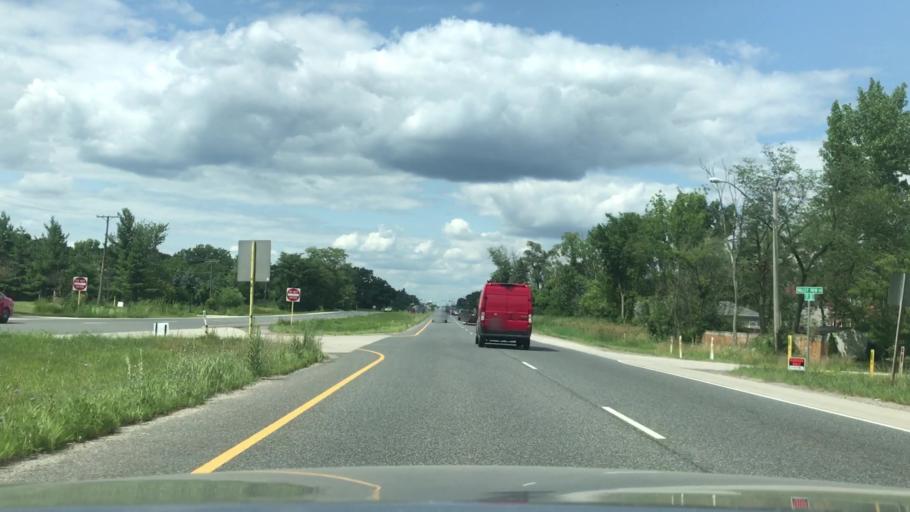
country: US
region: Illinois
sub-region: DuPage County
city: Burr Ridge
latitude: 41.7256
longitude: -87.9437
